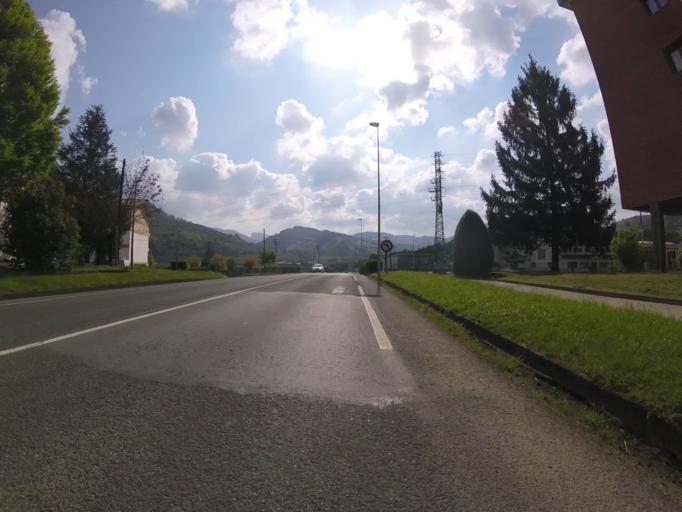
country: ES
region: Basque Country
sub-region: Provincia de Guipuzcoa
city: Azpeitia
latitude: 43.1787
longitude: -2.2652
